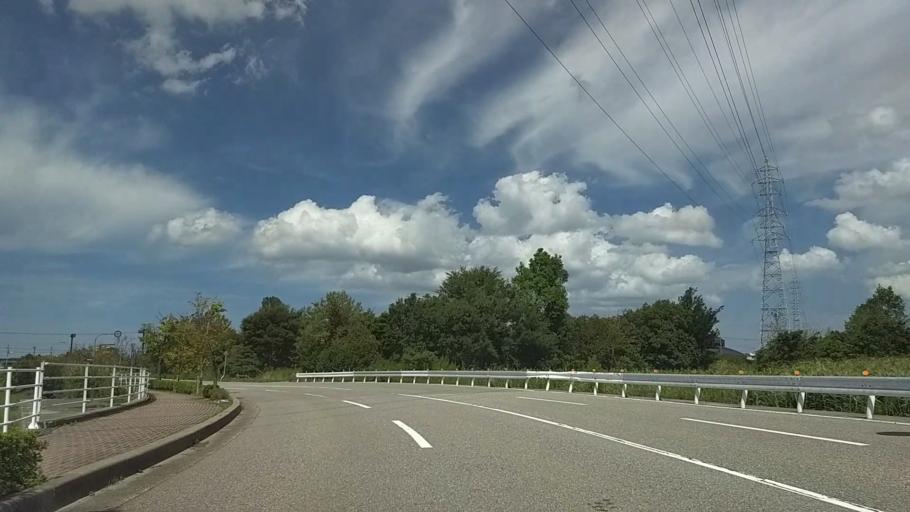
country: JP
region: Ishikawa
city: Kanazawa-shi
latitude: 36.5932
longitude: 136.6571
